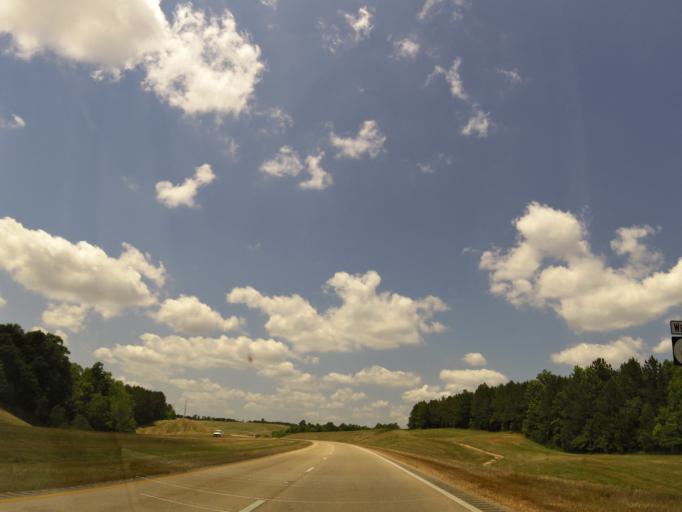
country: US
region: Mississippi
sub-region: Pontotoc County
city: Pontotoc
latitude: 34.2866
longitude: -88.9533
